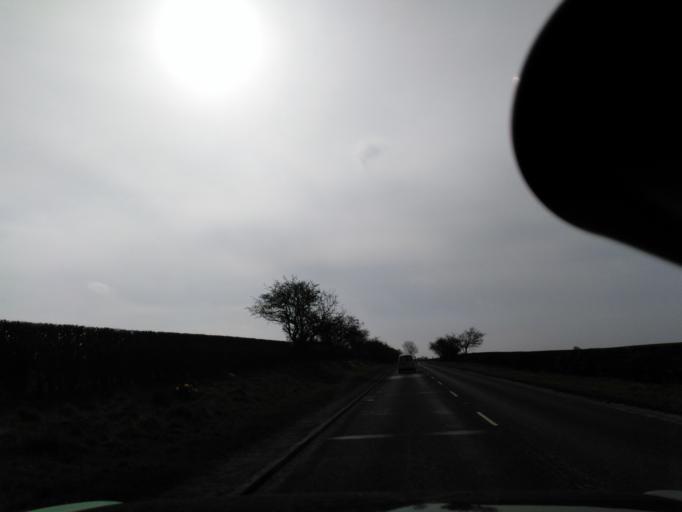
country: GB
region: England
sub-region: North Yorkshire
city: Northallerton
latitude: 54.3265
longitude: -1.4244
